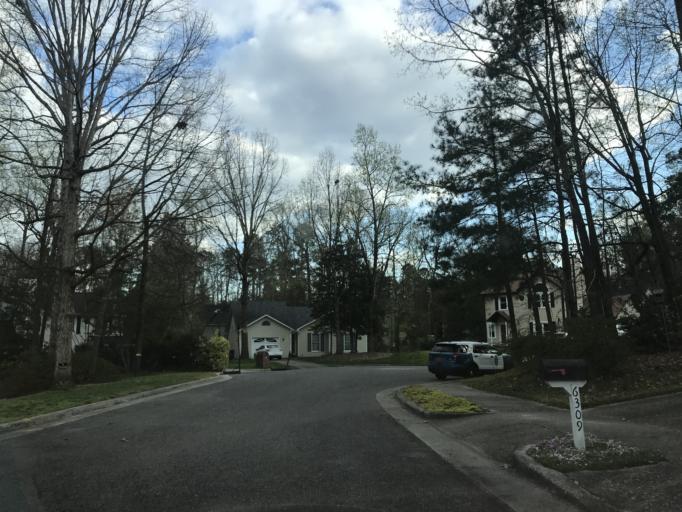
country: US
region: North Carolina
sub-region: Wake County
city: Knightdale
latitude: 35.8665
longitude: -78.5615
